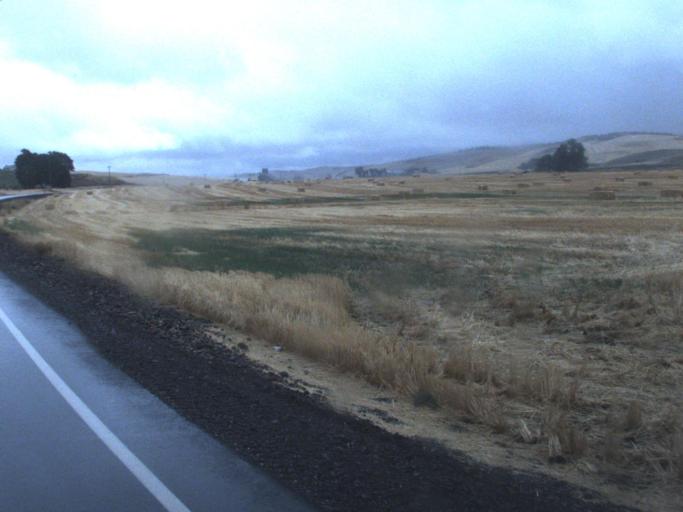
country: US
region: Washington
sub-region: Whitman County
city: Colfax
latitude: 47.0825
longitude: -117.5418
